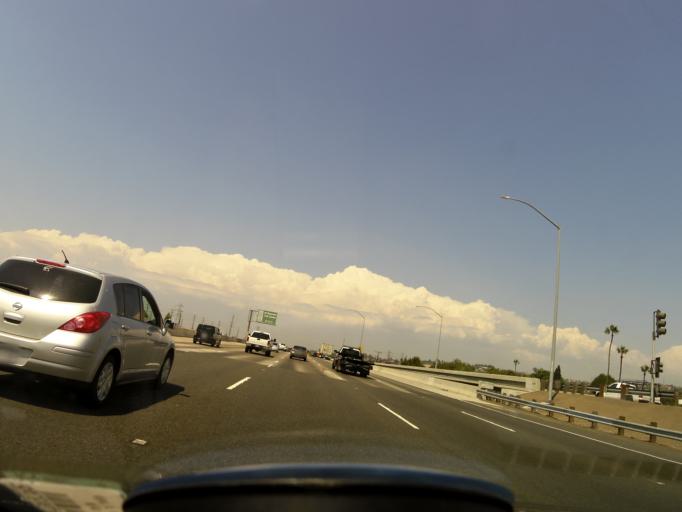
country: US
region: California
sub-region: Orange County
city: Villa Park
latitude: 33.8098
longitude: -117.8318
